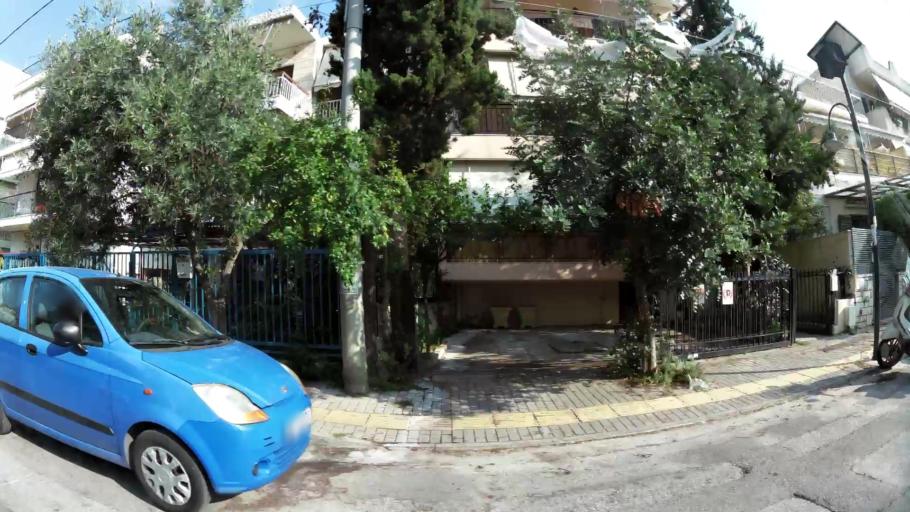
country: GR
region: Attica
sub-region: Nomarchia Athinas
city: Cholargos
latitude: 37.9992
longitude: 23.8108
